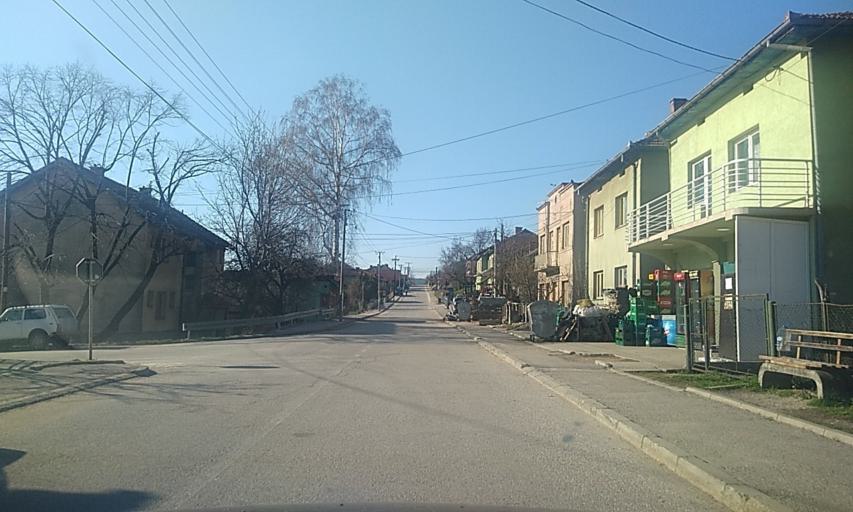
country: RS
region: Central Serbia
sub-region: Pcinjski Okrug
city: Bosilegrad
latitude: 42.4966
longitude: 22.4695
